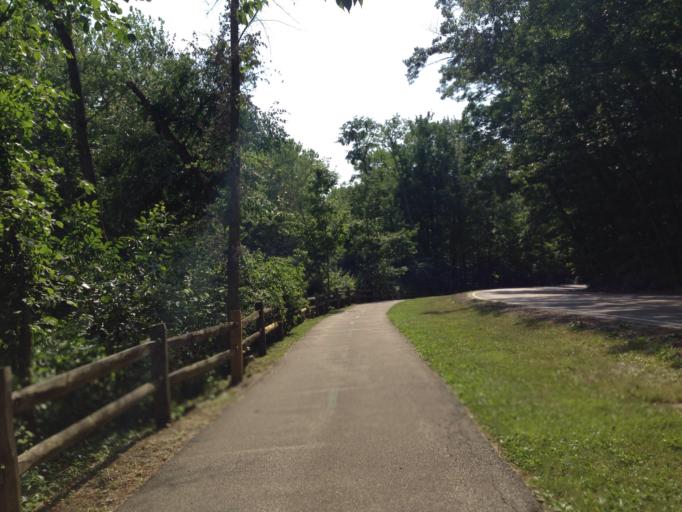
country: US
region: Ohio
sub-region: Cuyahoga County
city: Olmsted Falls
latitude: 41.3937
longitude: -81.8818
